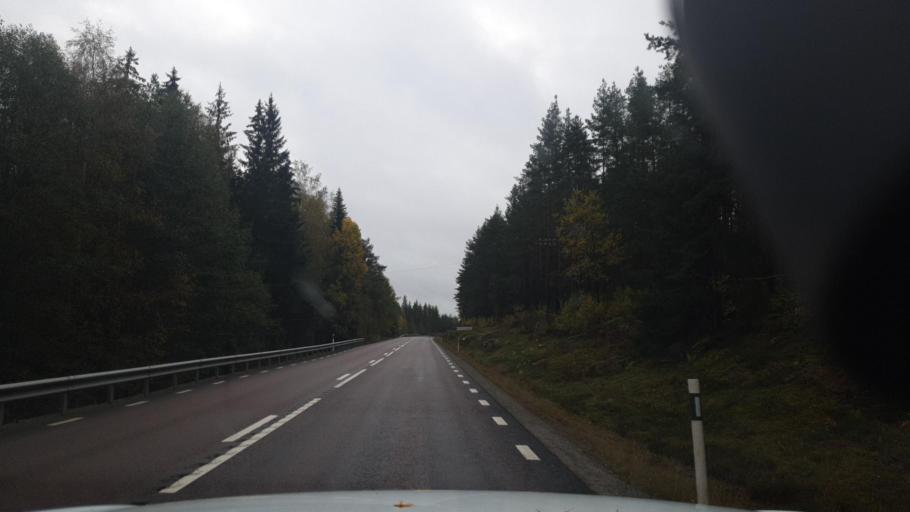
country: SE
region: Vaermland
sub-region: Karlstads Kommun
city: Edsvalla
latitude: 59.5980
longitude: 13.0040
